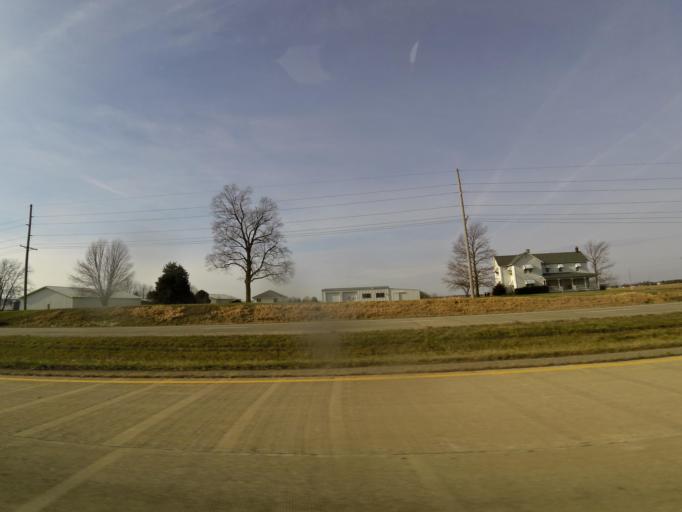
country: US
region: Illinois
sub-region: De Witt County
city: Clinton
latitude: 40.1166
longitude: -88.9651
